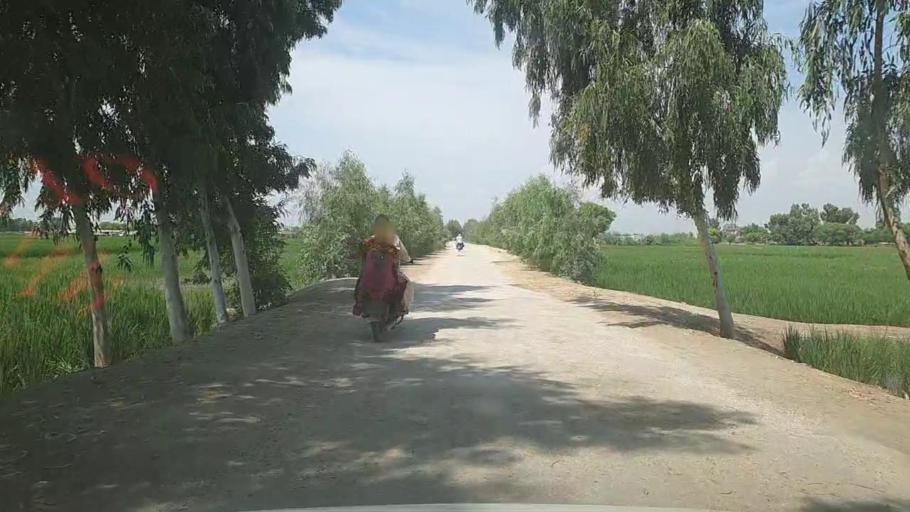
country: PK
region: Sindh
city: Kandhkot
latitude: 28.2930
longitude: 69.2378
